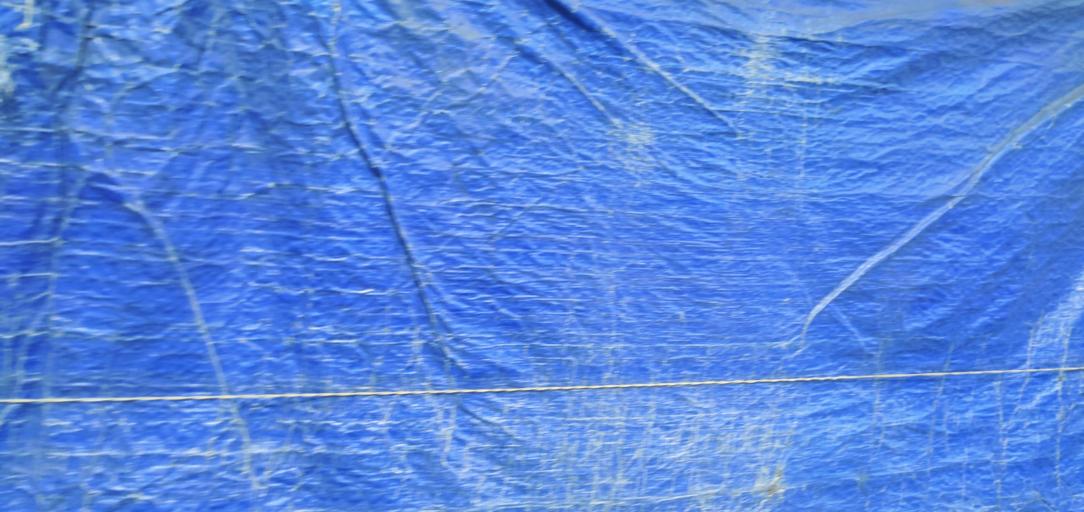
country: IN
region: Kerala
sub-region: Alappuzha
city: Kayankulam
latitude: 9.2262
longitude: 76.4589
